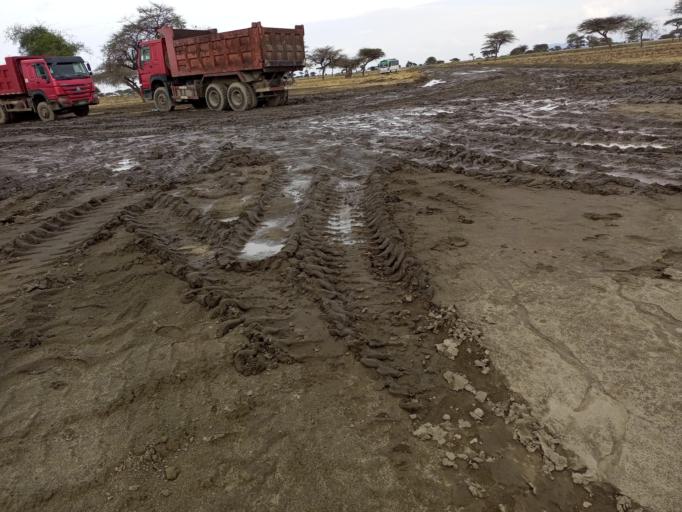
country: ET
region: Oromiya
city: Ziway
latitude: 7.9204
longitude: 38.6823
